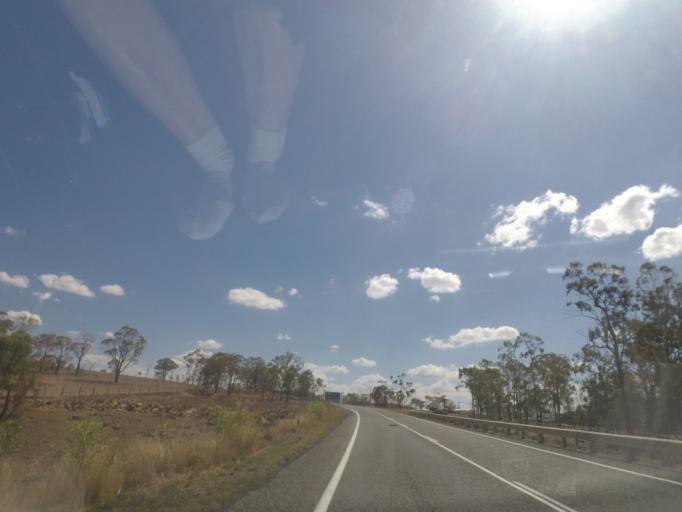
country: AU
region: Queensland
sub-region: Southern Downs
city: Warwick
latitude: -28.2066
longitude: 151.5684
